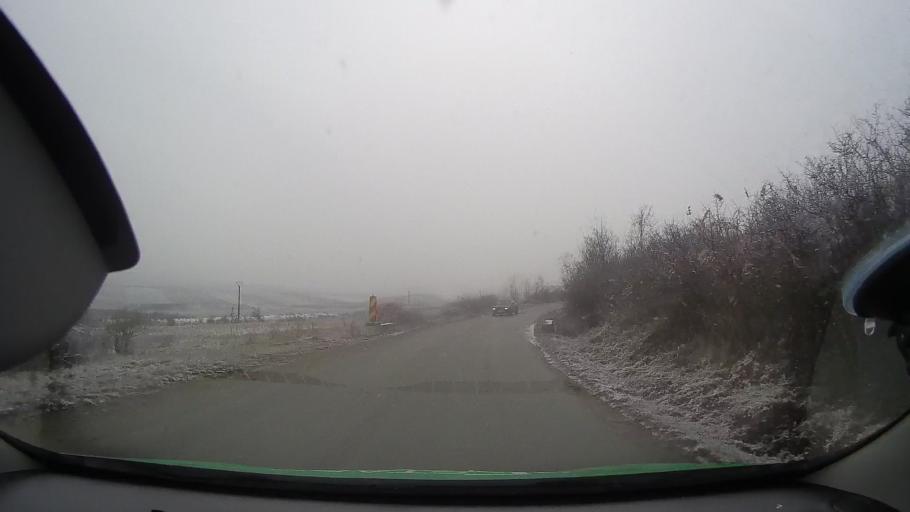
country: RO
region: Alba
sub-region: Comuna Noslac
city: Noslac
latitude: 46.3722
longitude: 23.9204
